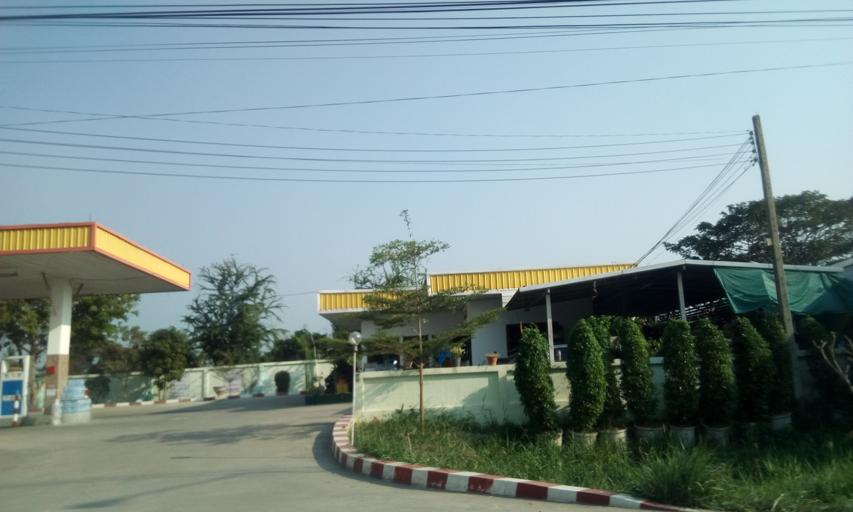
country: TH
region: Sing Buri
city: Sing Buri
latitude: 14.8573
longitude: 100.3913
